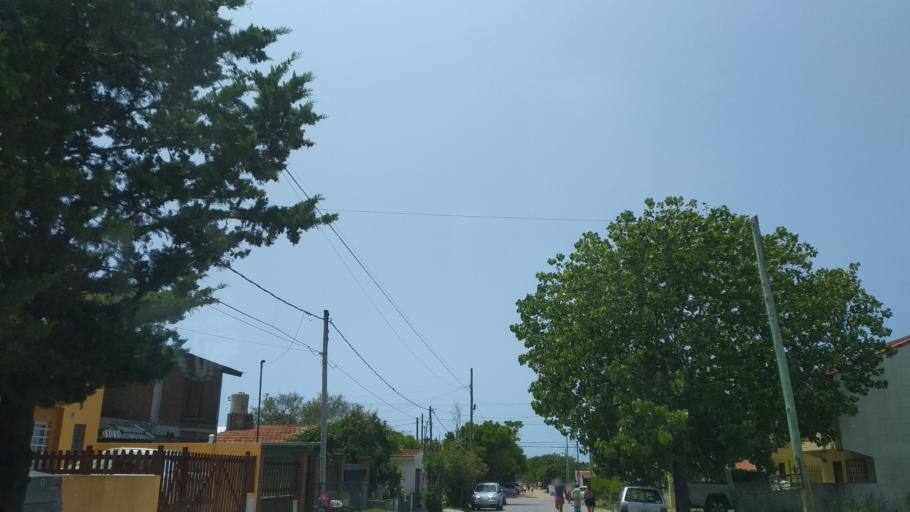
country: AR
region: Buenos Aires
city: Mar del Tuyu
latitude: -36.5569
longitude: -56.6904
